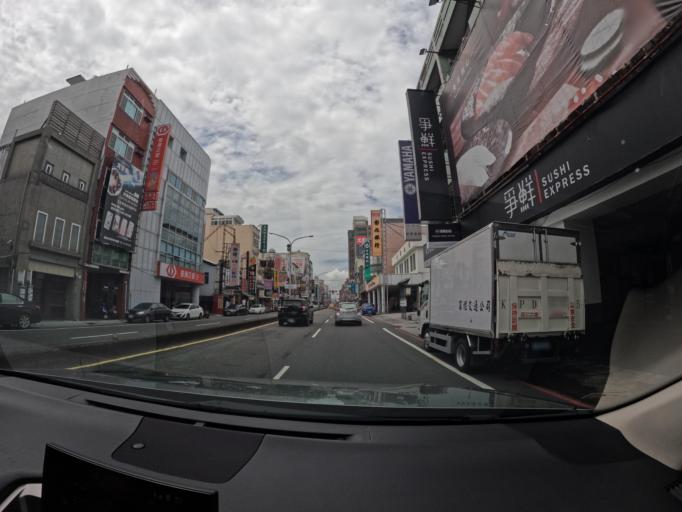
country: TW
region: Kaohsiung
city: Kaohsiung
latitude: 22.7955
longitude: 120.2956
